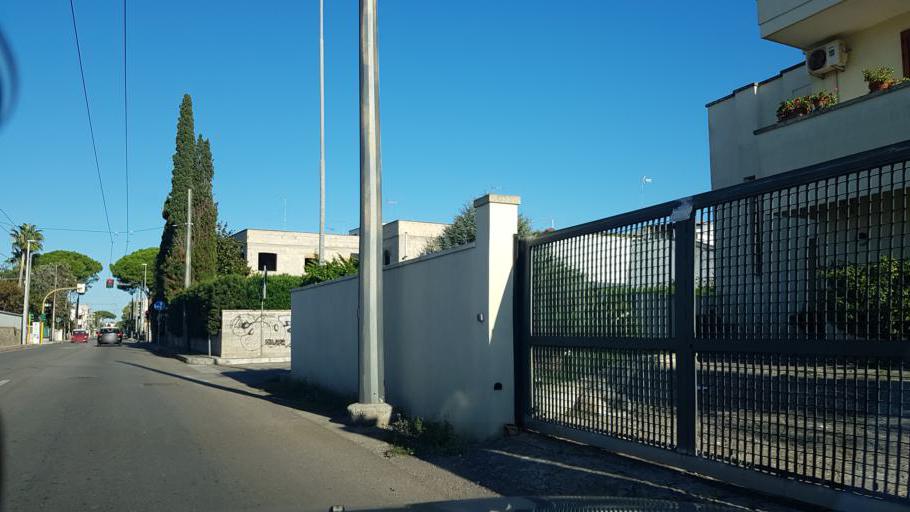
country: IT
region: Apulia
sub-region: Provincia di Lecce
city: Lecce
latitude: 40.3437
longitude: 18.1436
